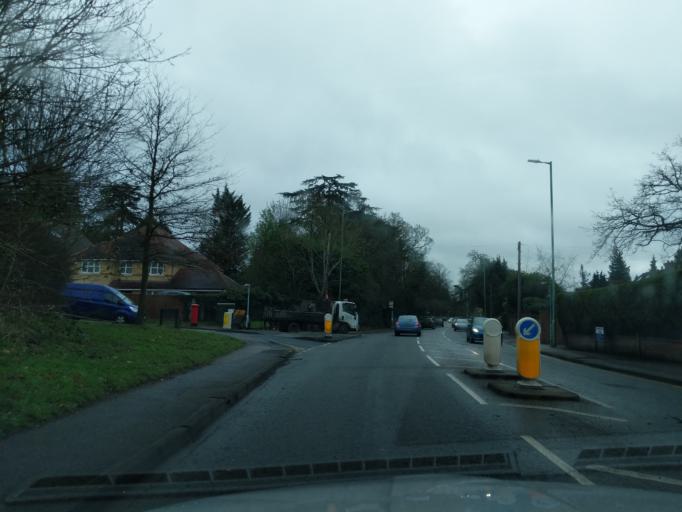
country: GB
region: England
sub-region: Hertfordshire
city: Watford
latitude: 51.6743
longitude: -0.4189
